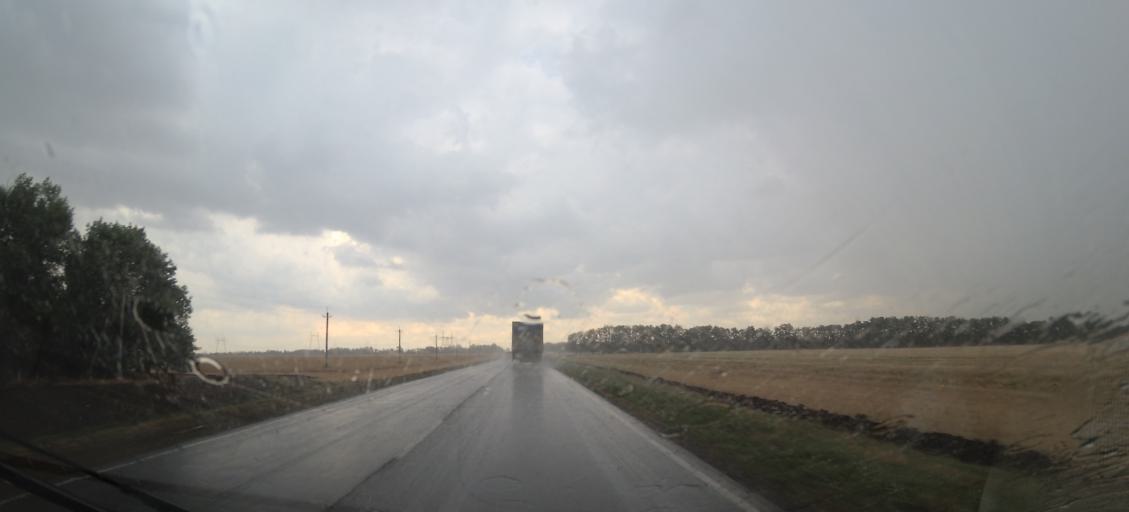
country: RU
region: Rostov
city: Gundorovskiy
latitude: 46.8603
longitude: 41.9468
